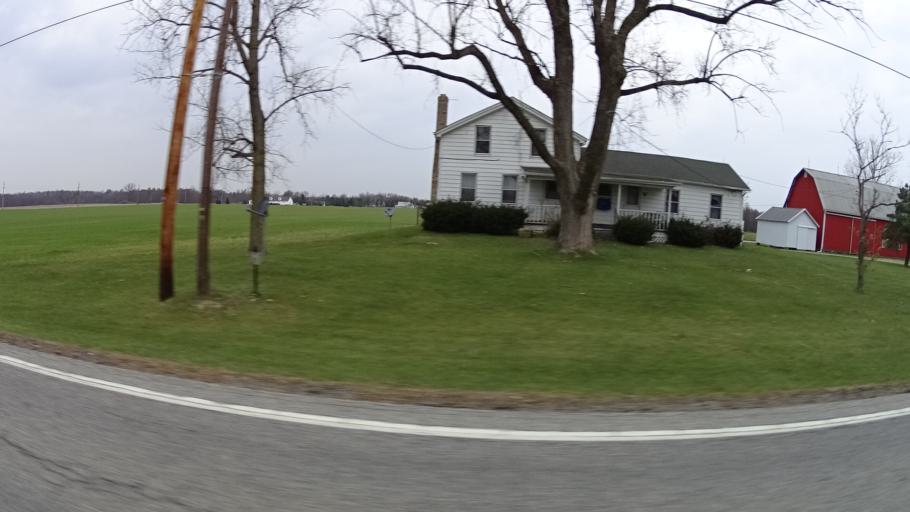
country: US
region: Ohio
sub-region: Lorain County
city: Grafton
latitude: 41.2379
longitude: -82.0596
